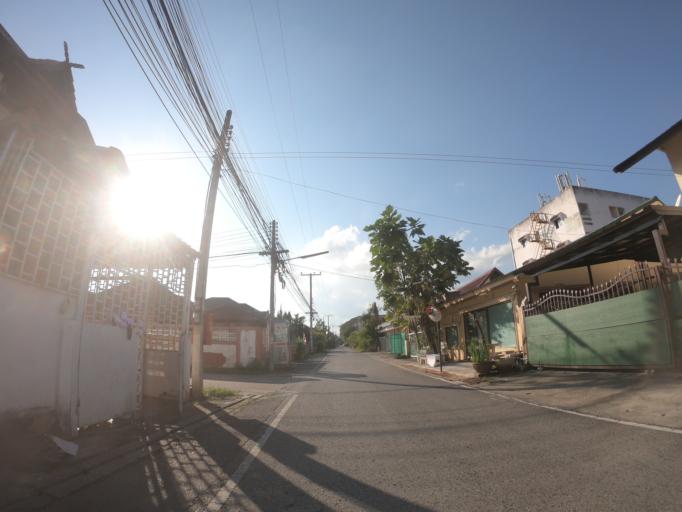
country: TH
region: Chiang Mai
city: Chiang Mai
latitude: 18.7540
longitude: 98.9699
